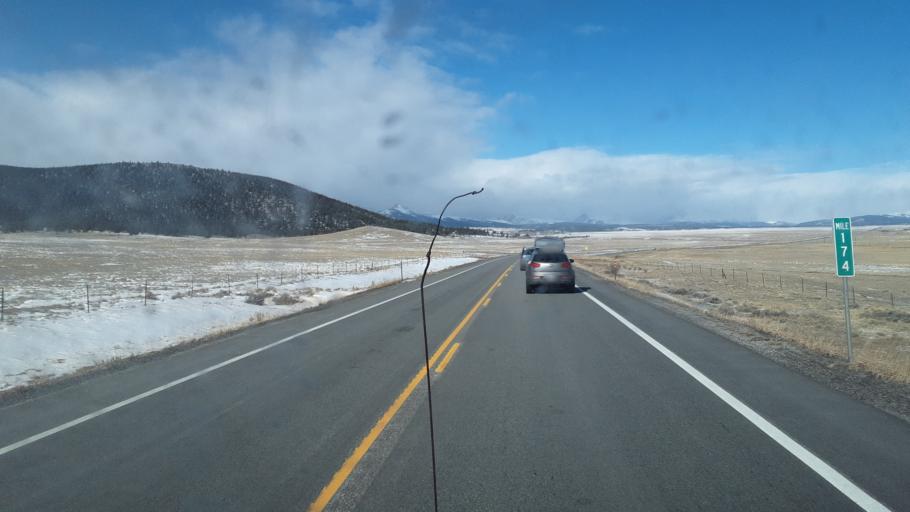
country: US
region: Colorado
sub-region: Park County
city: Fairplay
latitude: 39.0925
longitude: -105.9851
